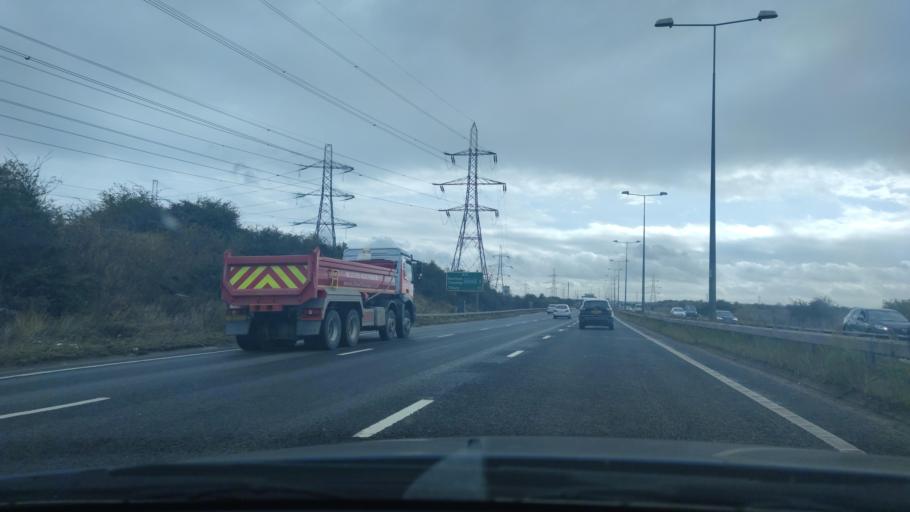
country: GB
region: England
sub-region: Greater London
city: Erith
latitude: 51.5086
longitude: 0.2010
